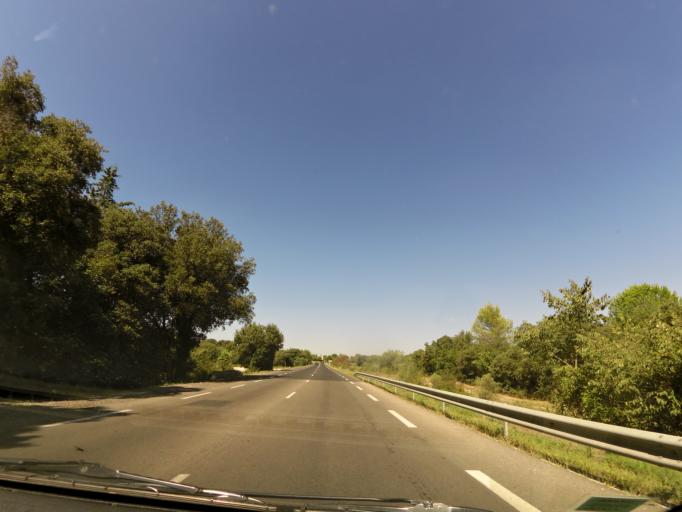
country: FR
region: Languedoc-Roussillon
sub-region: Departement du Gard
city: Villevieille
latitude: 43.7905
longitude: 4.1059
